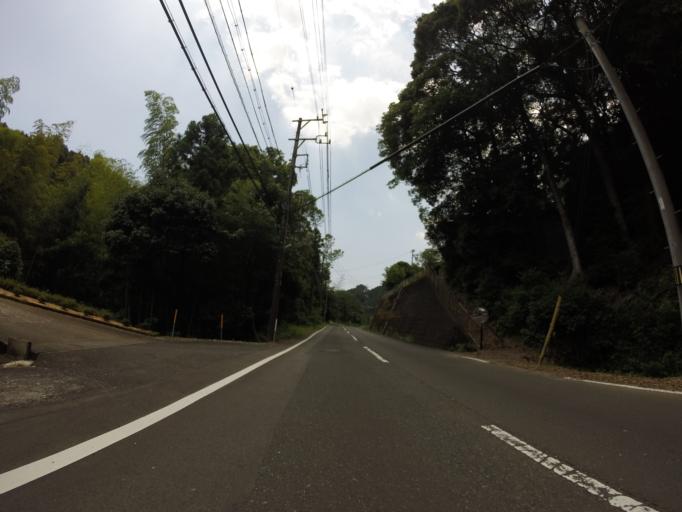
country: JP
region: Shizuoka
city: Kanaya
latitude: 34.8210
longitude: 138.0696
